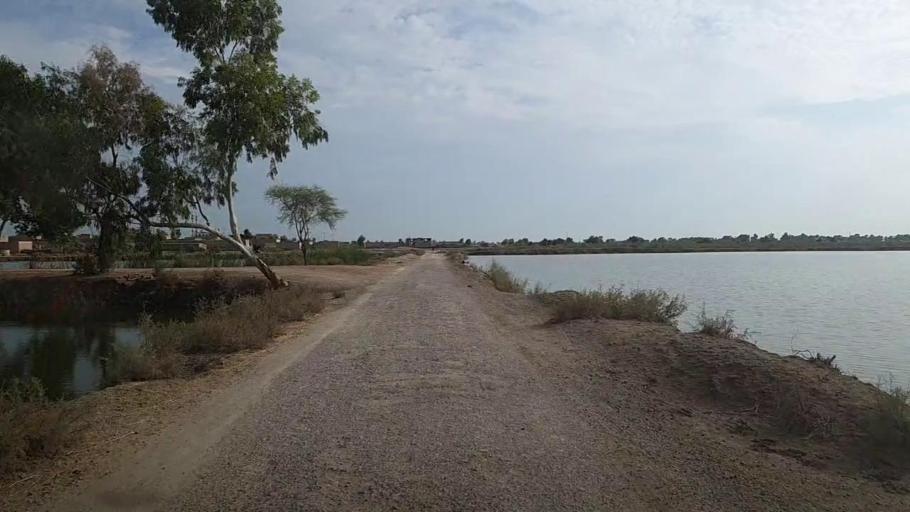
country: PK
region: Sindh
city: Thul
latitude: 28.2712
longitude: 68.8538
